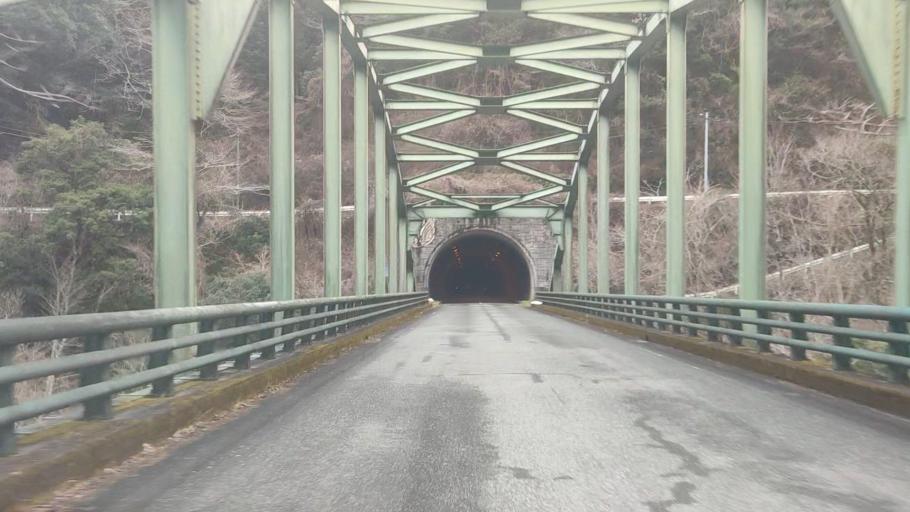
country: JP
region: Kumamoto
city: Matsubase
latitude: 32.5089
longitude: 130.9217
